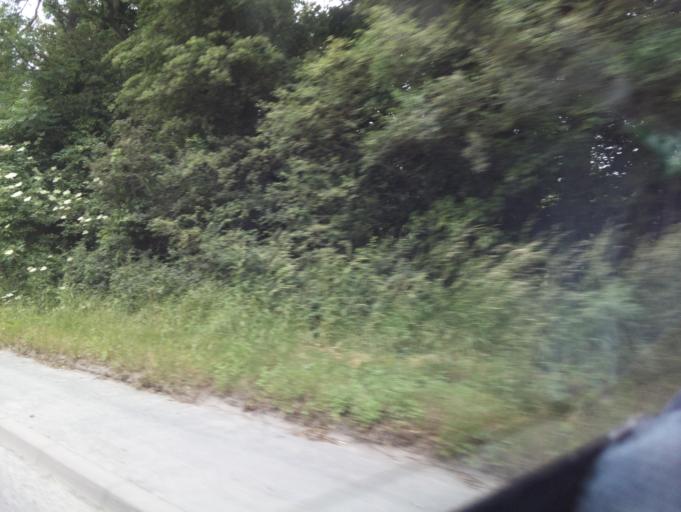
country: GB
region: England
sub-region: Leicestershire
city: Coalville
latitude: 52.7057
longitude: -1.3283
